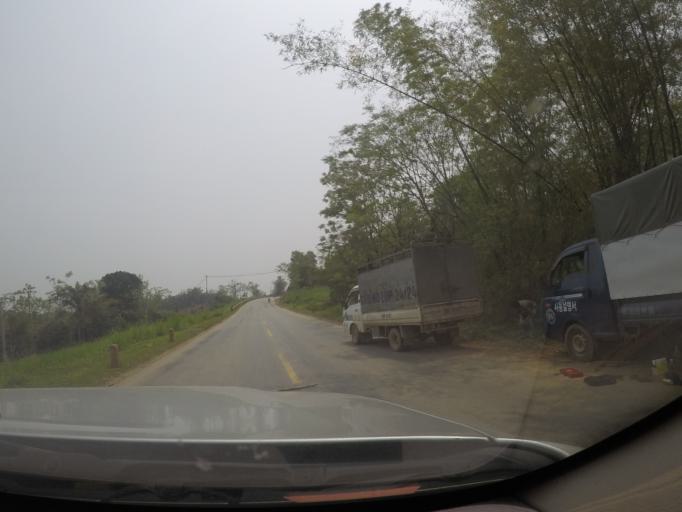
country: VN
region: Thanh Hoa
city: Thi Tran Thuong Xuan
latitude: 19.9548
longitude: 105.4030
